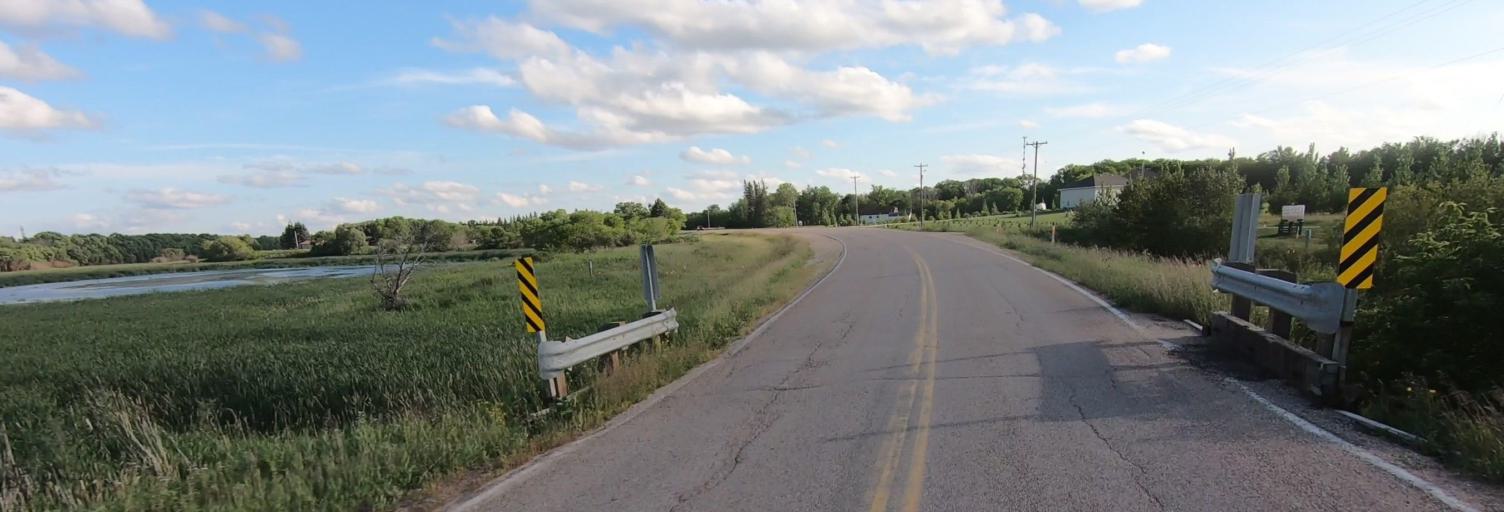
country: CA
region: Manitoba
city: Selkirk
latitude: 50.2129
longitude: -96.8414
